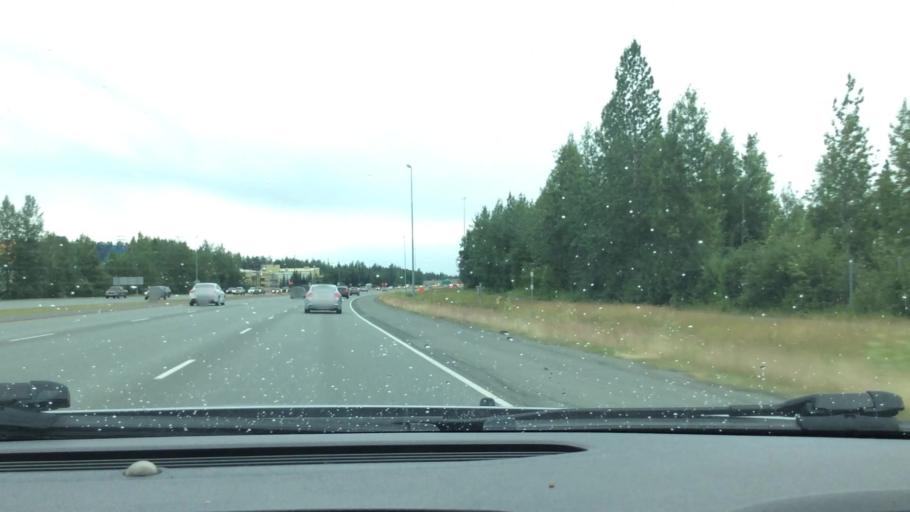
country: US
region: Alaska
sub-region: Anchorage Municipality
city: Elmendorf Air Force Base
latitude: 61.2327
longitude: -149.7104
